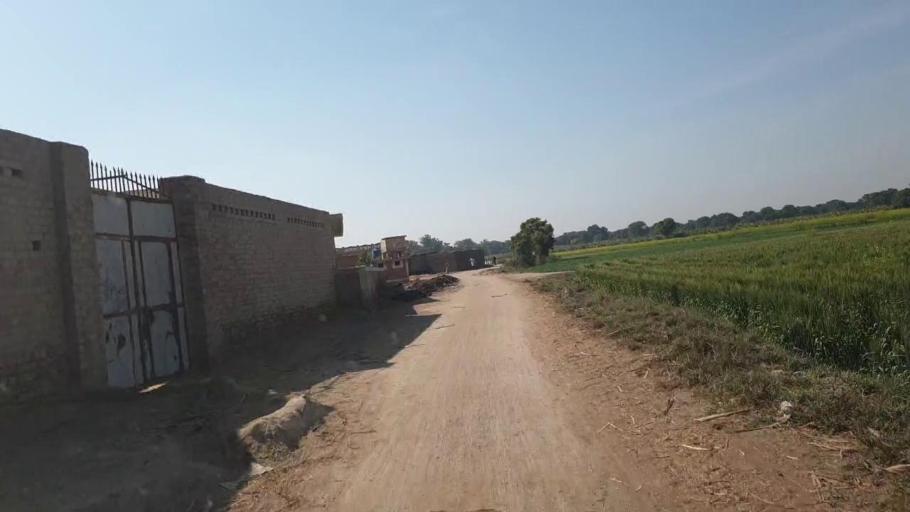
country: PK
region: Sindh
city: Tando Allahyar
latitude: 25.3909
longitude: 68.7816
